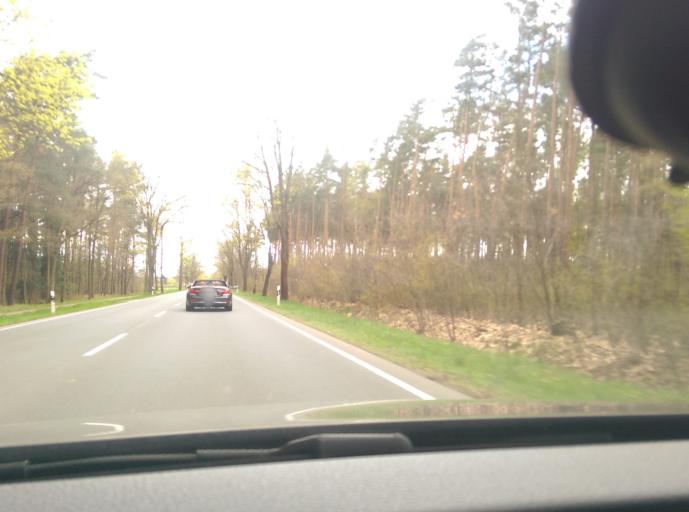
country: DE
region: Lower Saxony
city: Wietze
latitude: 52.6420
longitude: 9.8787
